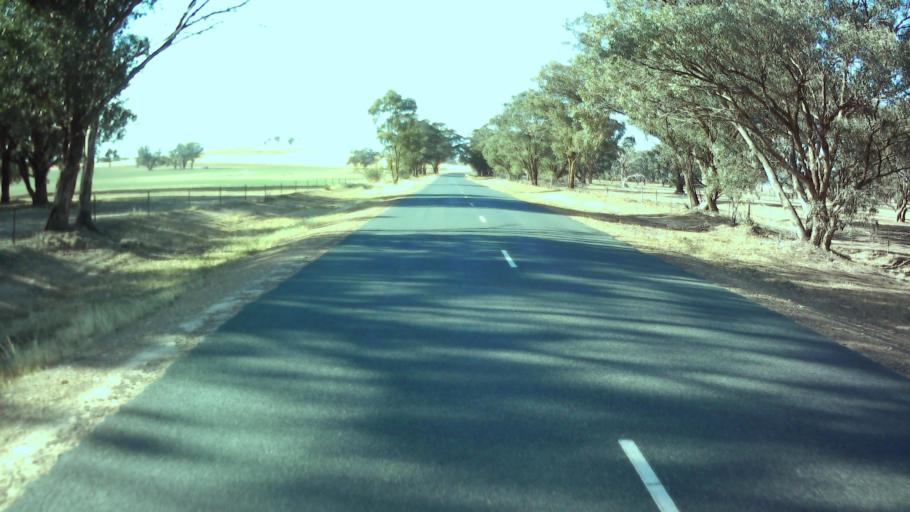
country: AU
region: New South Wales
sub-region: Weddin
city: Grenfell
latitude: -33.9642
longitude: 148.1404
